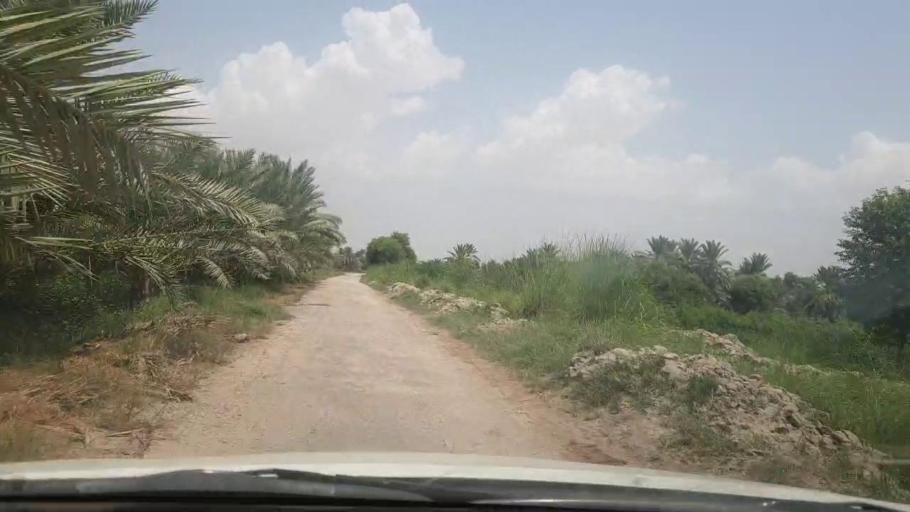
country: PK
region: Sindh
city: Khairpur
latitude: 27.5487
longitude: 68.8438
